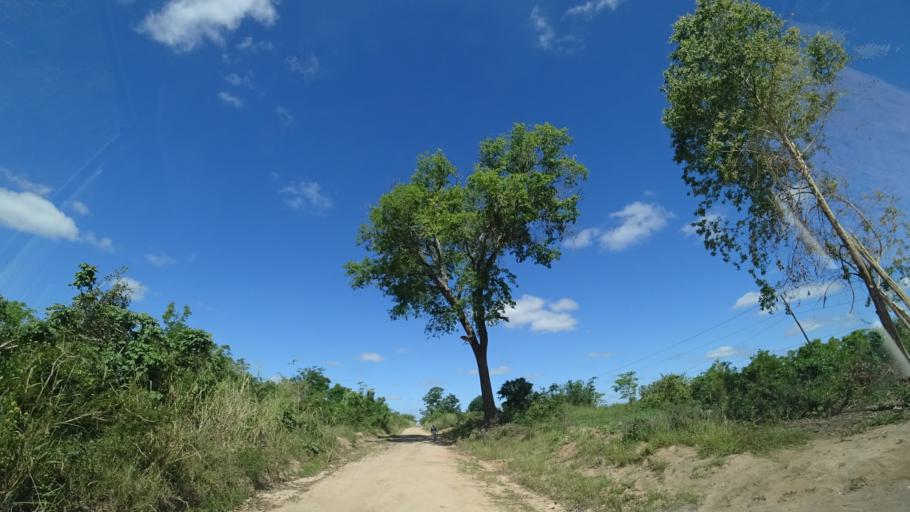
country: MZ
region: Sofala
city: Dondo
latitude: -19.3212
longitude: 34.6915
